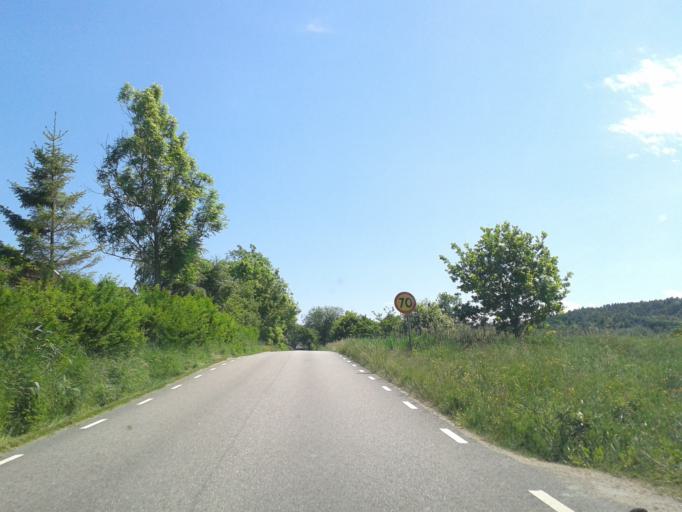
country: SE
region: Vaestra Goetaland
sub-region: Stenungsunds Kommun
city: Stora Hoga
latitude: 58.0258
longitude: 11.8749
